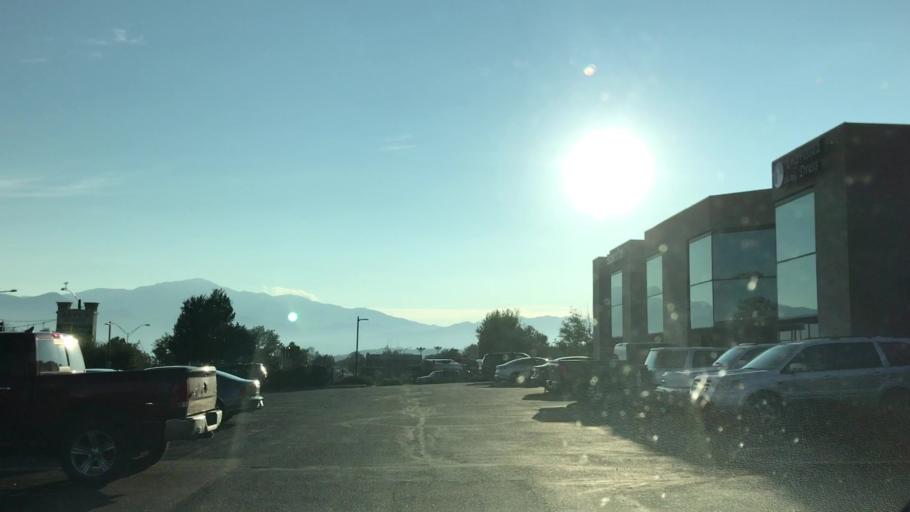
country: US
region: Colorado
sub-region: El Paso County
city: Cimarron Hills
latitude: 38.8974
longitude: -104.7442
